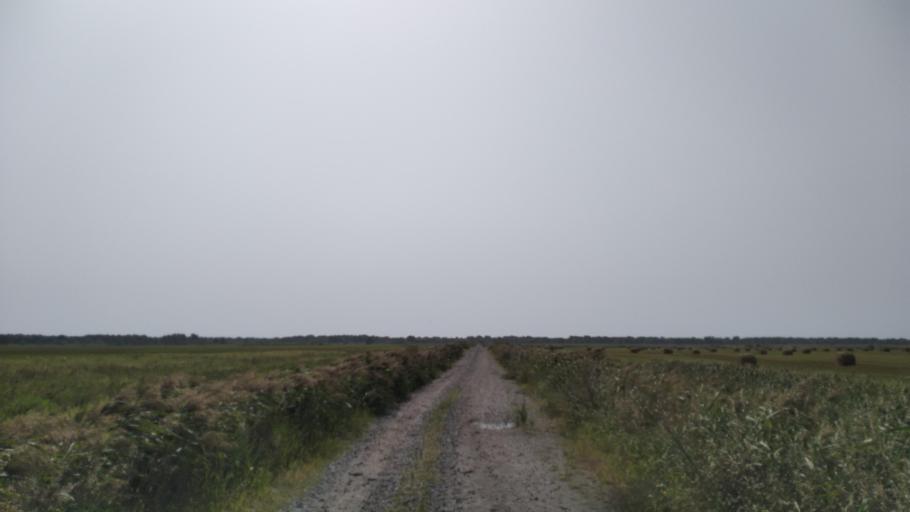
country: BY
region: Brest
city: Davyd-Haradok
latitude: 51.9810
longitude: 27.1749
